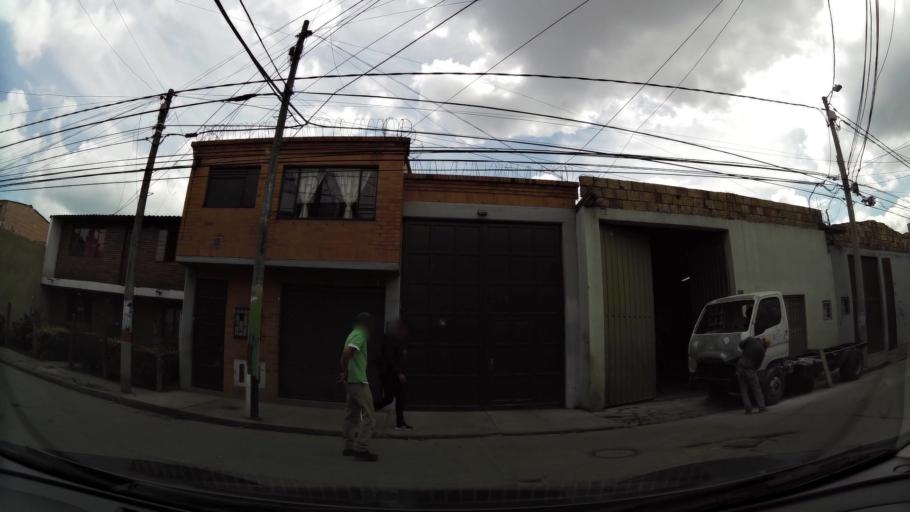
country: CO
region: Cundinamarca
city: Cota
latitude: 4.7236
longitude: -74.0939
